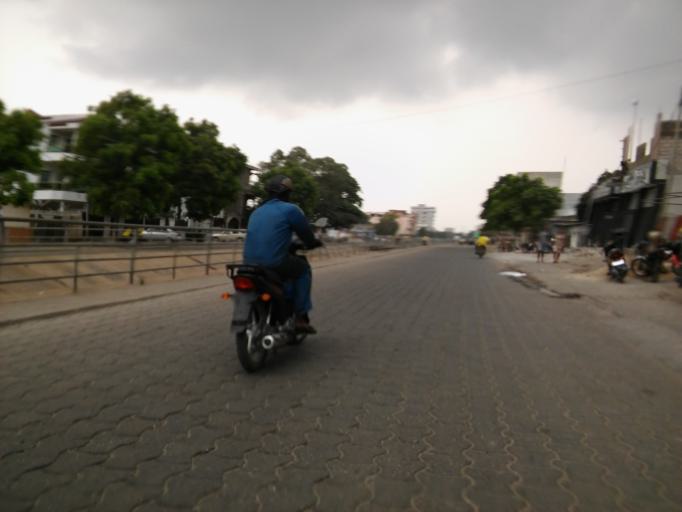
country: BJ
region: Littoral
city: Cotonou
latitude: 6.3779
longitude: 2.4178
